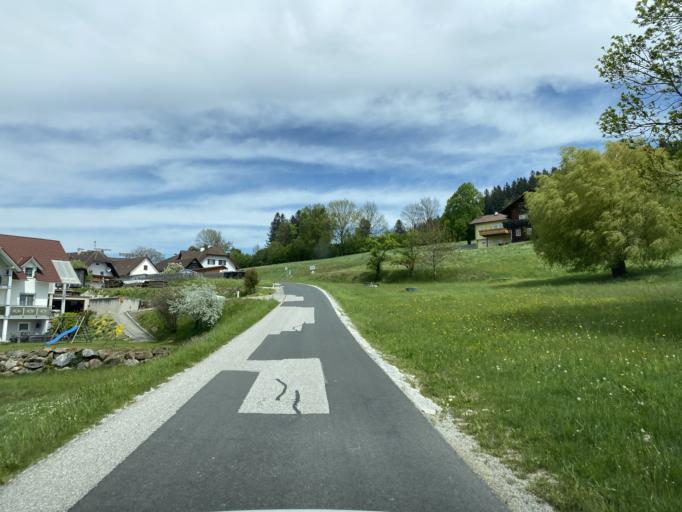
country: AT
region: Styria
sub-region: Politischer Bezirk Weiz
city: Gschaid bei Birkfeld
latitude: 47.3537
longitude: 15.7212
